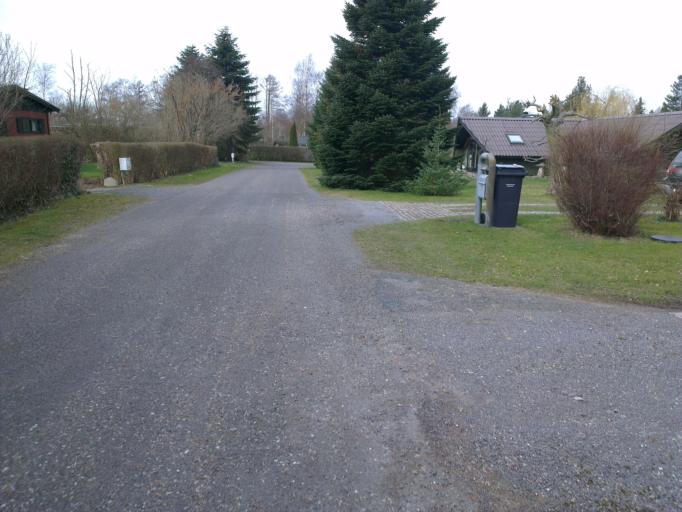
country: DK
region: Capital Region
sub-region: Frederikssund Kommune
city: Jaegerspris
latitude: 55.8105
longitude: 11.9446
